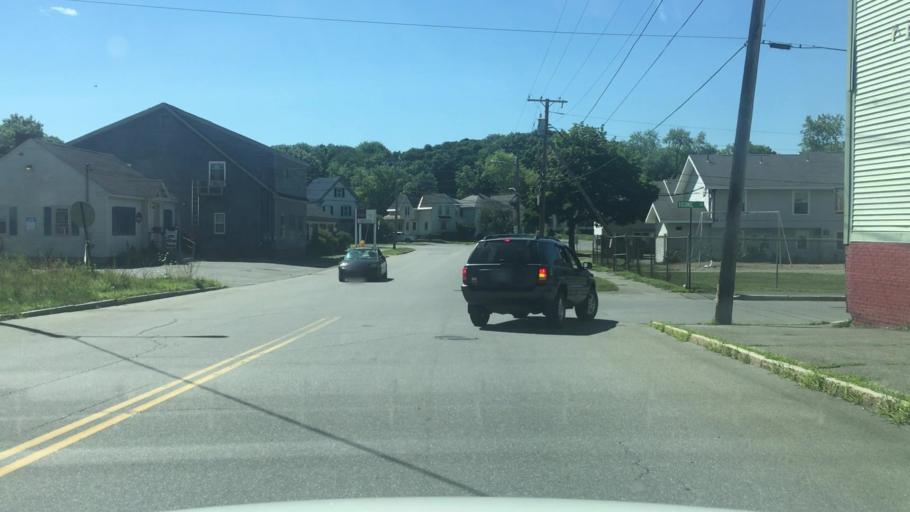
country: US
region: Maine
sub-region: Kennebec County
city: Waterville
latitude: 44.5577
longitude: -69.6307
